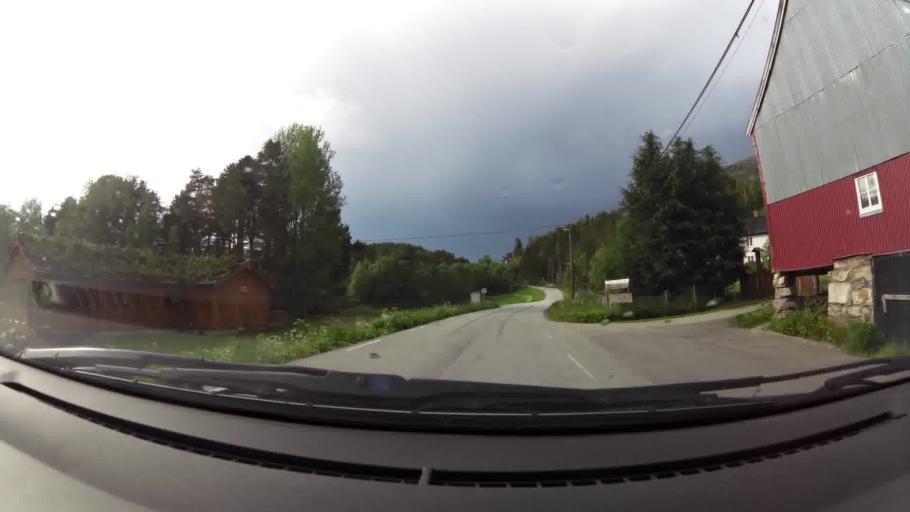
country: NO
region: More og Romsdal
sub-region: Kristiansund
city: Kristiansund
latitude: 63.0304
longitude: 7.7398
